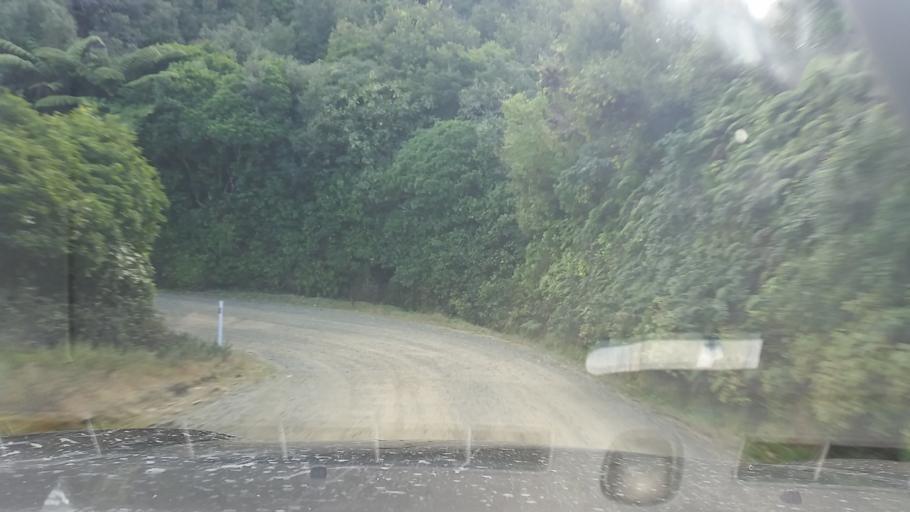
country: NZ
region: Marlborough
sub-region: Marlborough District
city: Picton
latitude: -41.1254
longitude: 174.1372
